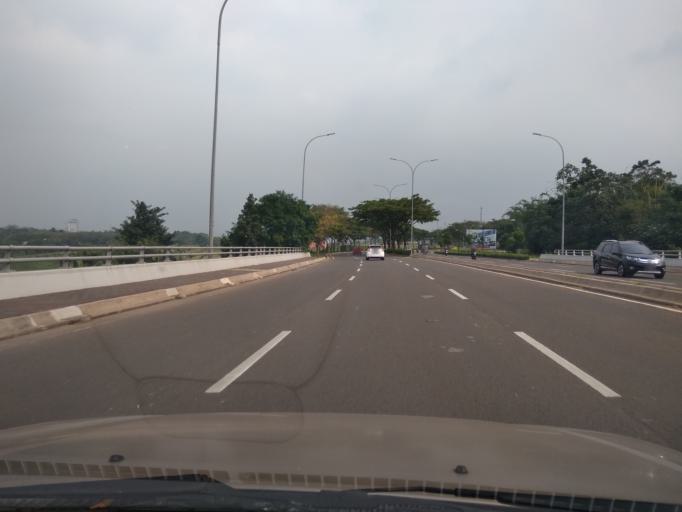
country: ID
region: West Java
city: Serpong
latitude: -6.2856
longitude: 106.6544
